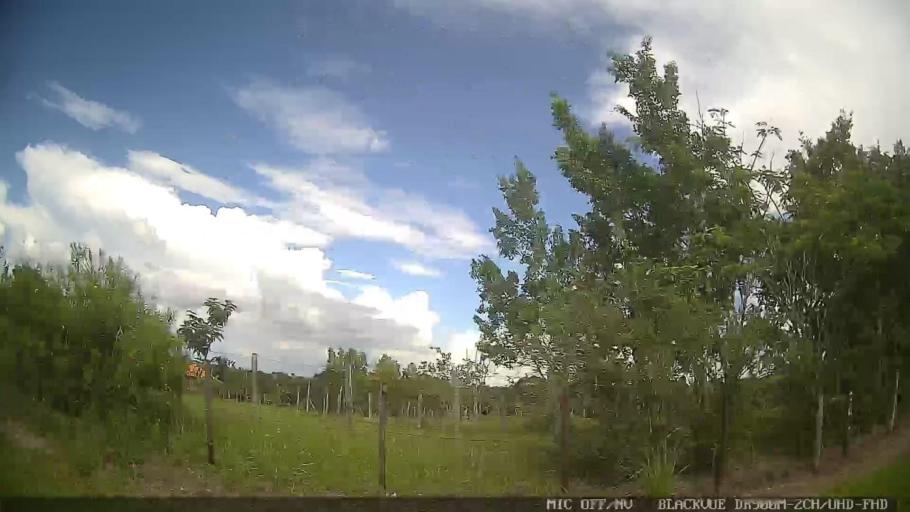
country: BR
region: Sao Paulo
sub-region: Conchas
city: Conchas
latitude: -22.9642
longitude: -47.9828
